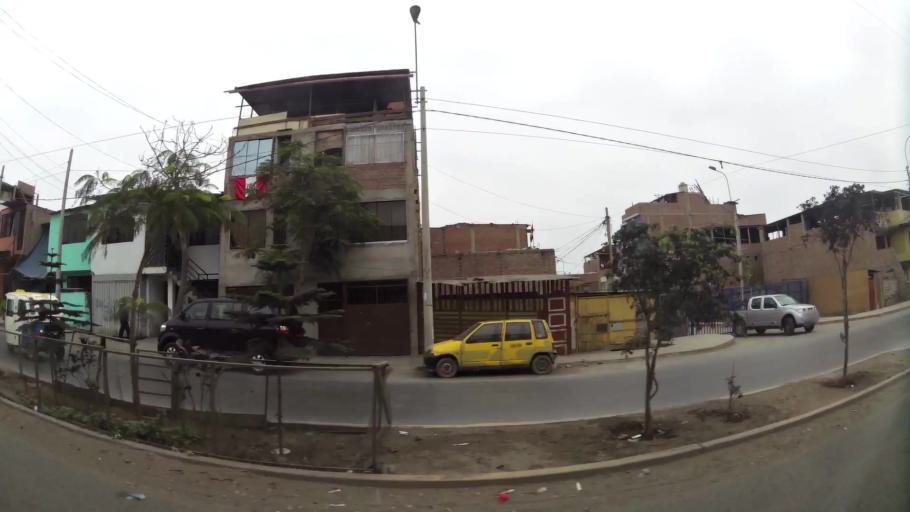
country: PE
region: Lima
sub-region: Lima
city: Surco
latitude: -12.2129
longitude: -76.9419
